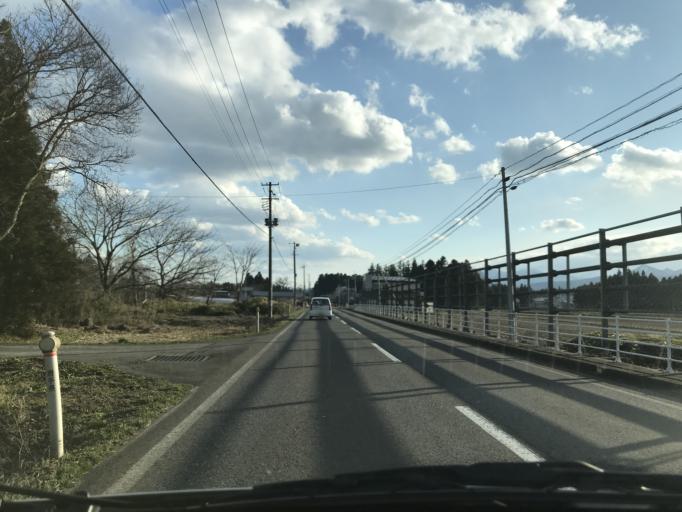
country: JP
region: Iwate
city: Kitakami
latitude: 39.3209
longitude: 141.0360
